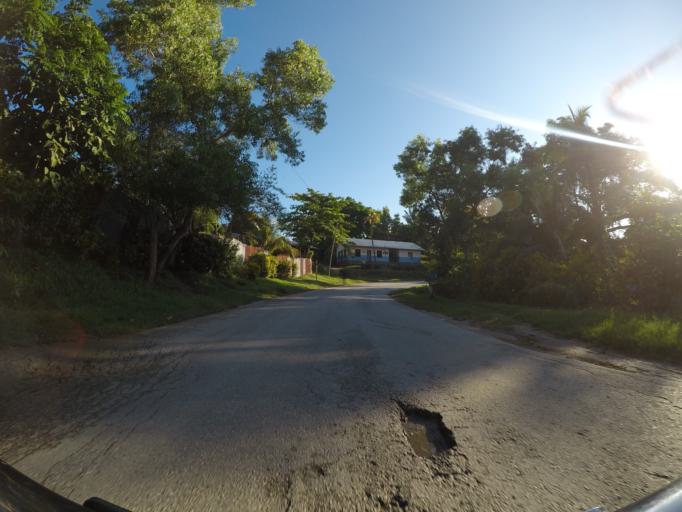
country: TZ
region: Pemba South
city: Mtambile
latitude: -5.3797
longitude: 39.6975
